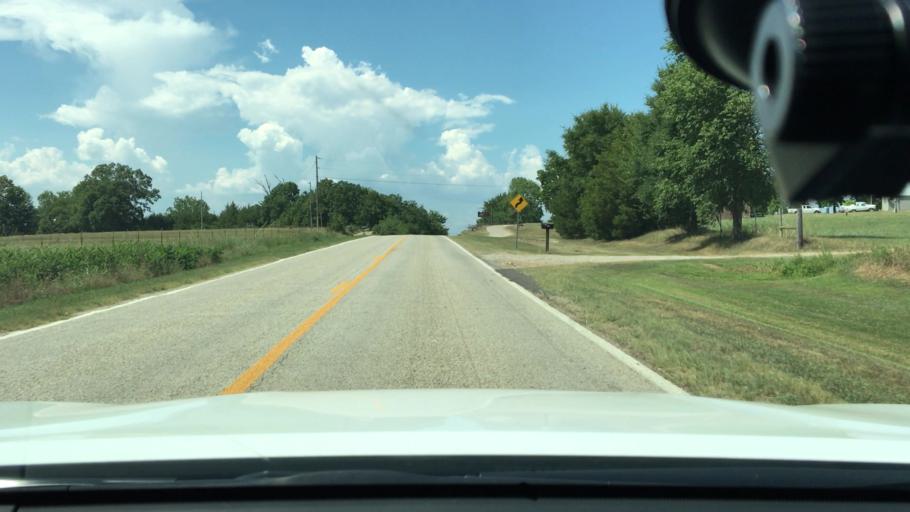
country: US
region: Arkansas
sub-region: Logan County
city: Paris
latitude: 35.3113
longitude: -93.6326
